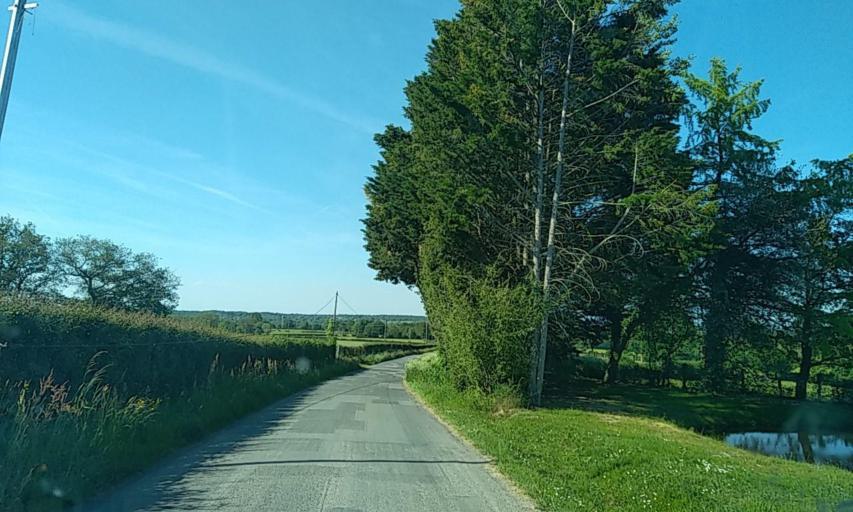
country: FR
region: Poitou-Charentes
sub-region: Departement des Deux-Sevres
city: Boisme
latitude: 46.8068
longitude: -0.4156
